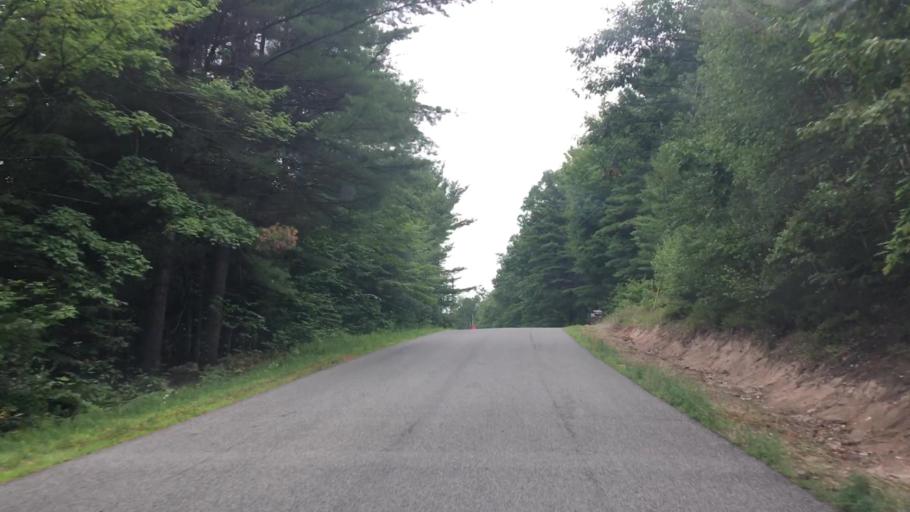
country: US
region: New York
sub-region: Essex County
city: Keeseville
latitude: 44.4508
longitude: -73.5949
